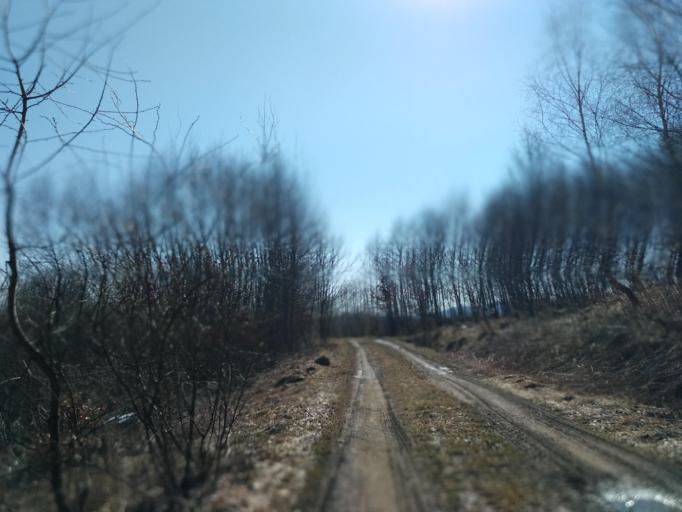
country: PL
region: Subcarpathian Voivodeship
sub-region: Powiat brzozowski
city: Domaradz
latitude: 49.8035
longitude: 21.9591
